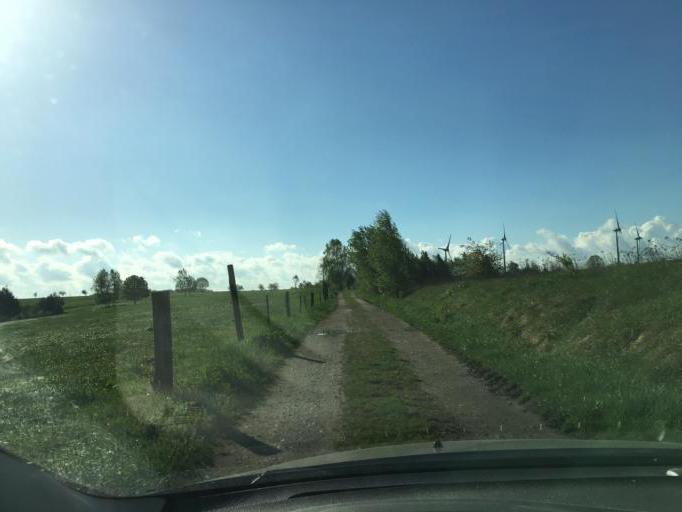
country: DE
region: Saxony
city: Narsdorf
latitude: 50.9921
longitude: 12.7140
